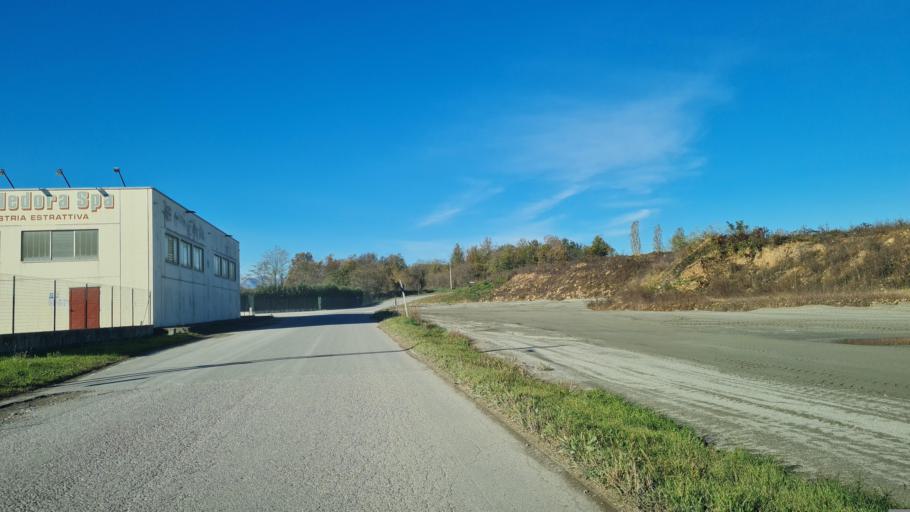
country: IT
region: Piedmont
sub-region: Provincia di Biella
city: Cavaglia
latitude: 45.3868
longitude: 8.0882
